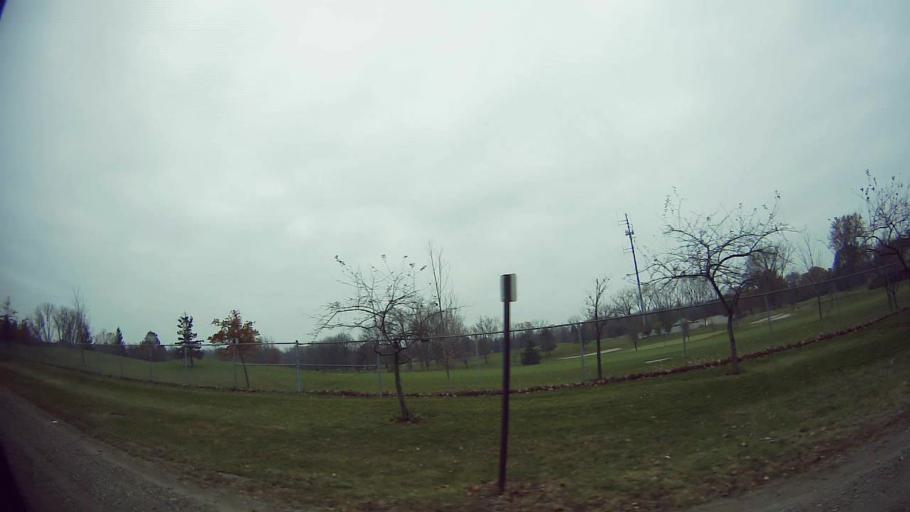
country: US
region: Michigan
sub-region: Oakland County
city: Beverly Hills
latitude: 42.5355
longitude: -83.2456
